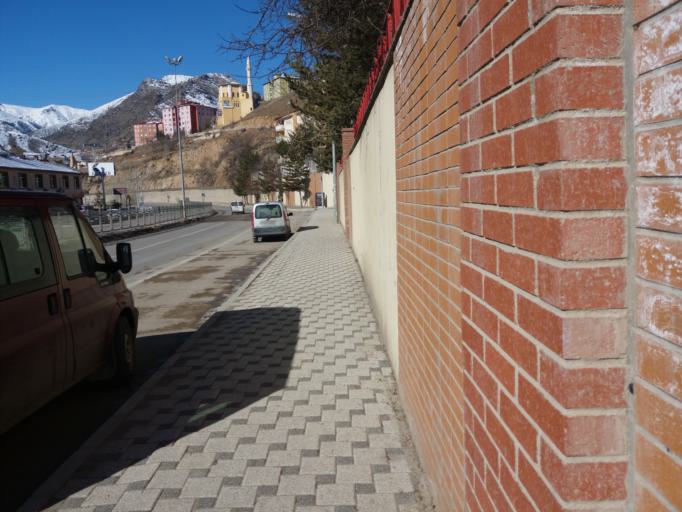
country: TR
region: Gumushane
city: Gumushkhane
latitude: 40.4363
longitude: 39.5137
